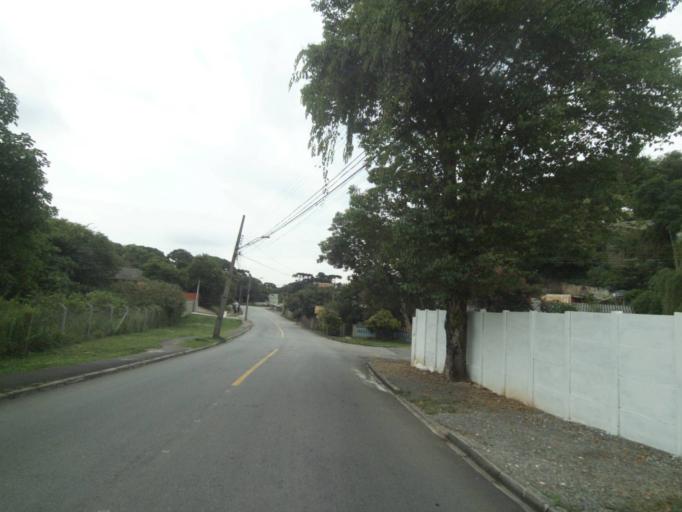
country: BR
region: Parana
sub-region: Curitiba
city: Curitiba
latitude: -25.4133
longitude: -49.3001
